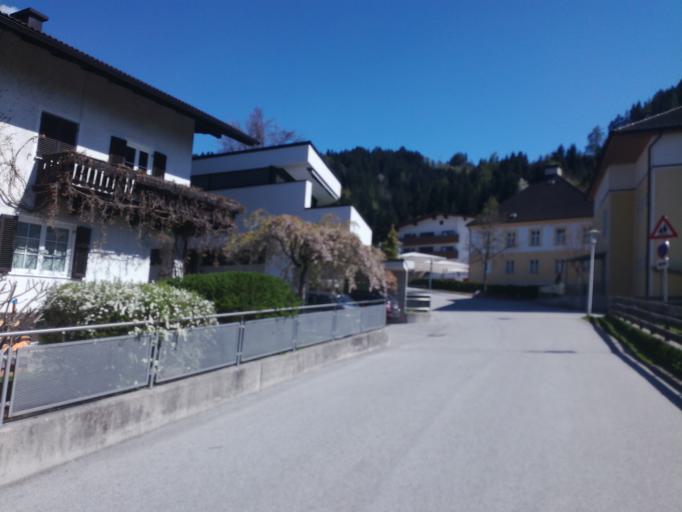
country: AT
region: Tyrol
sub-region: Politischer Bezirk Schwaz
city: Pill
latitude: 47.3211
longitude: 11.6808
